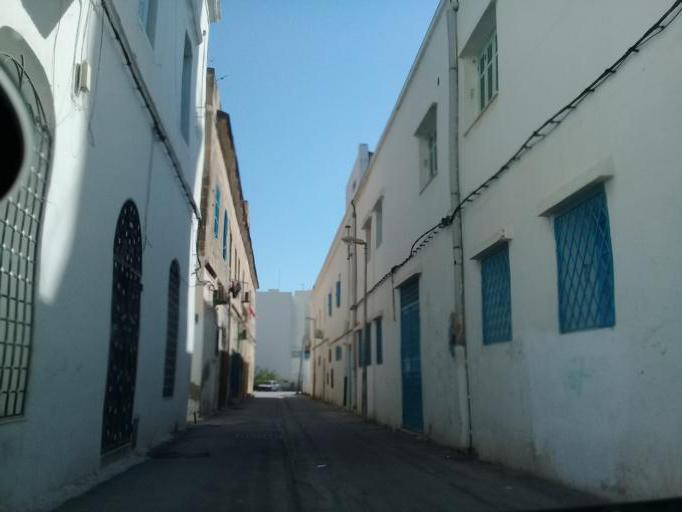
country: TN
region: Tunis
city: La Goulette
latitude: 36.8163
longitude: 10.3021
